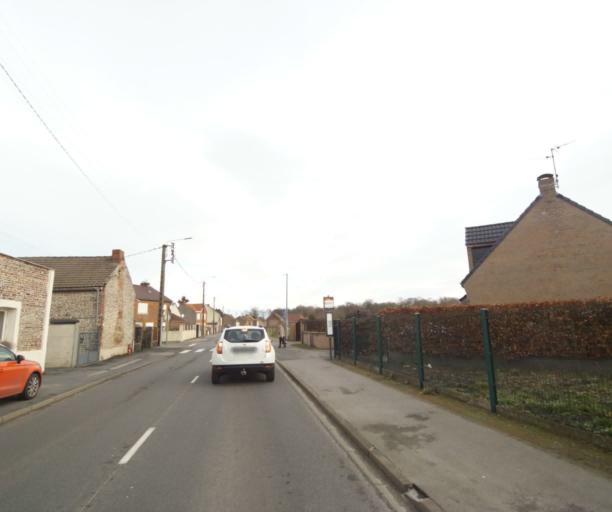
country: FR
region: Nord-Pas-de-Calais
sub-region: Departement du Nord
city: Vieux-Conde
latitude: 50.4823
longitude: 3.5800
